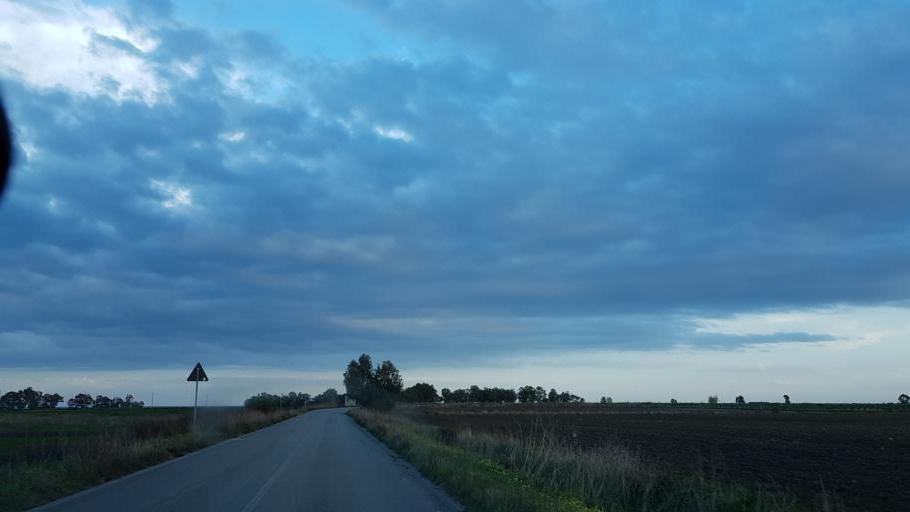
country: IT
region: Apulia
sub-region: Provincia di Brindisi
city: La Rosa
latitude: 40.5855
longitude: 18.0304
